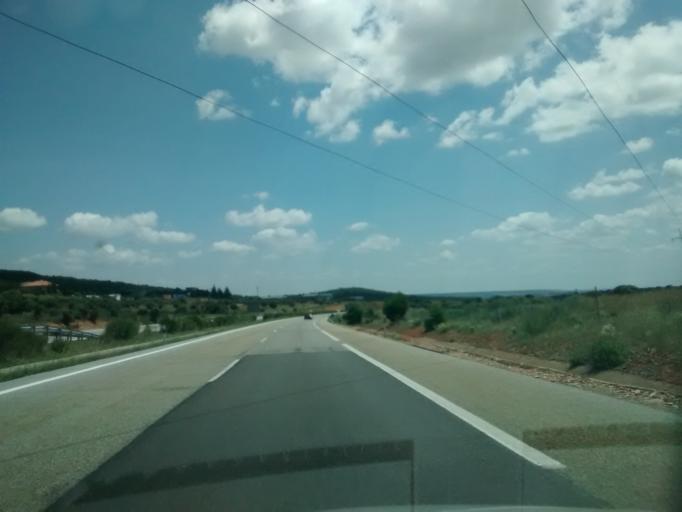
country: ES
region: Castille and Leon
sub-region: Provincia de Leon
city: Brazuelo
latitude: 42.4845
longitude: -6.1174
